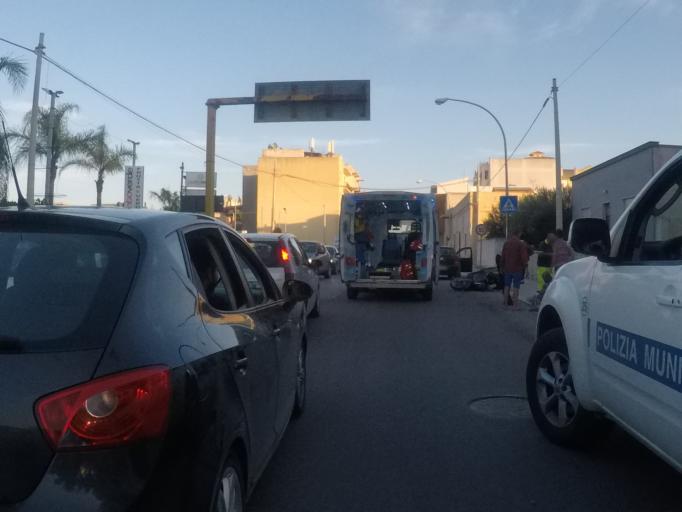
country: IT
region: Sicily
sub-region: Trapani
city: Petrosino
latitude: 37.7810
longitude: 12.4564
